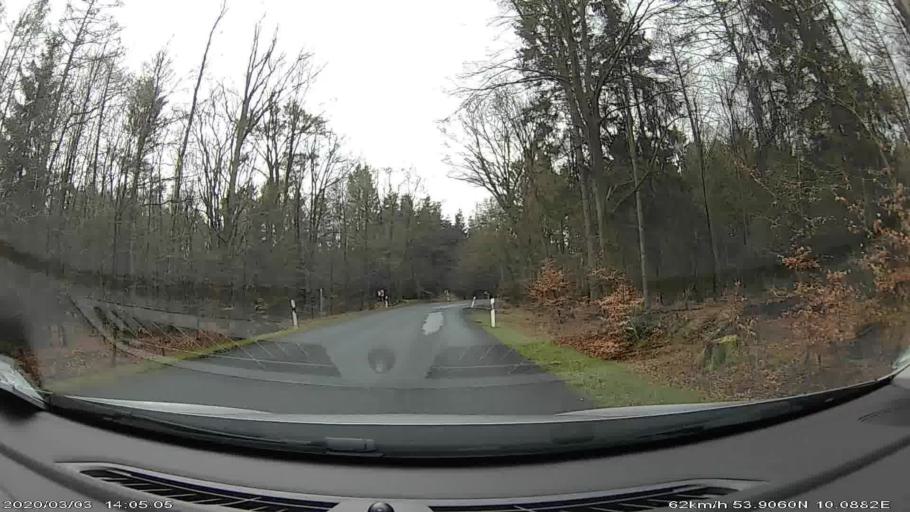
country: DE
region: Schleswig-Holstein
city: Hartenholm
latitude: 53.9055
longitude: 10.0879
